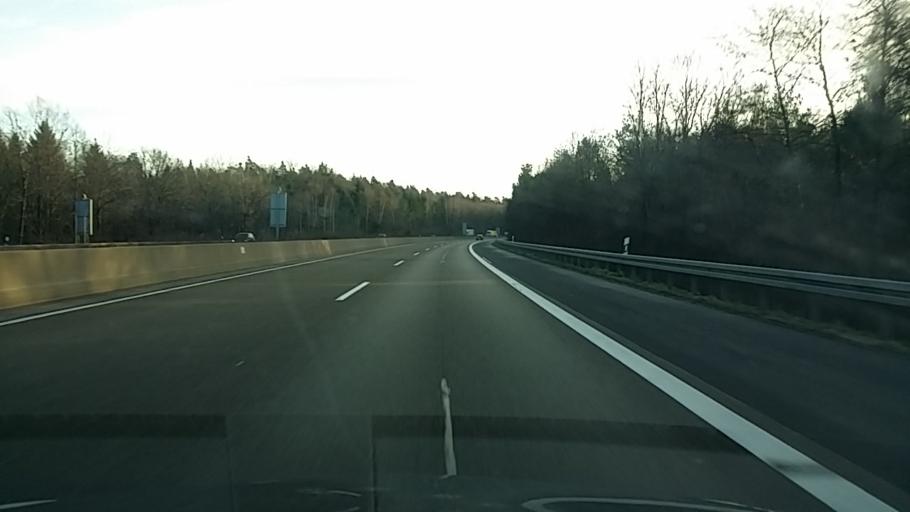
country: DE
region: Hesse
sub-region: Regierungsbezirk Kassel
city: Petersberg
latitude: 50.6173
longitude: 9.6812
